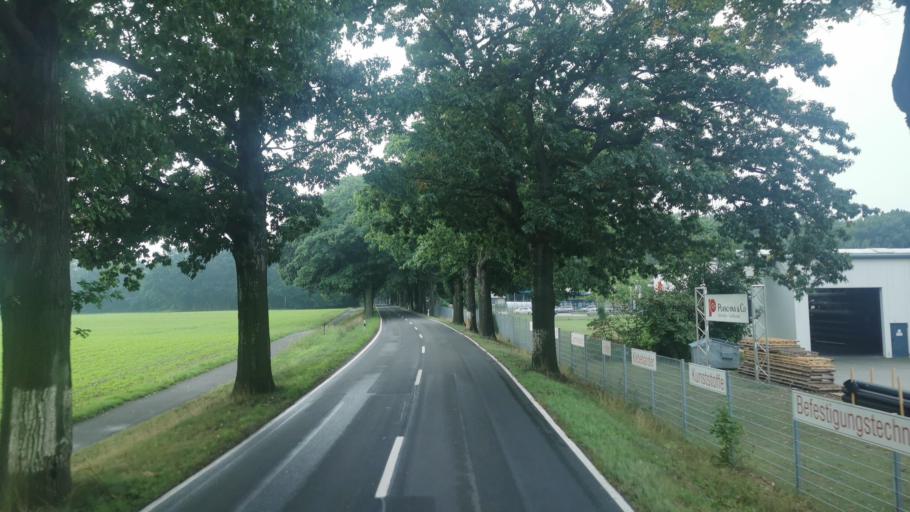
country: DE
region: Brandenburg
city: Kolkwitz
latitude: 51.7381
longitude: 14.2598
